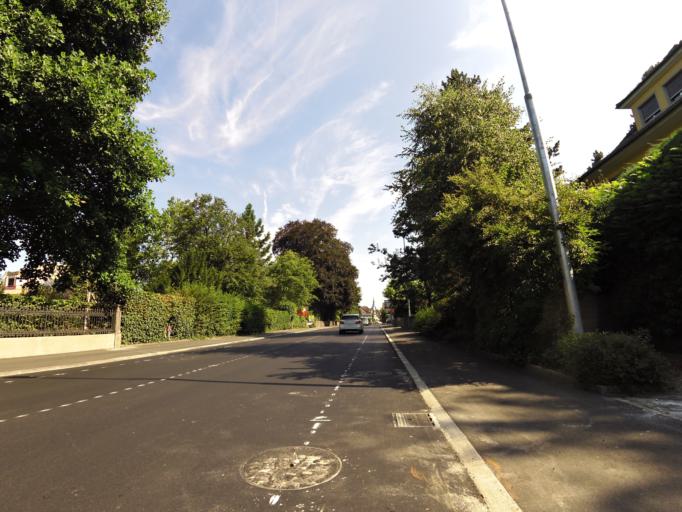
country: CH
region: Zug
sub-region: Zug
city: Zug
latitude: 47.1627
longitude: 8.5137
